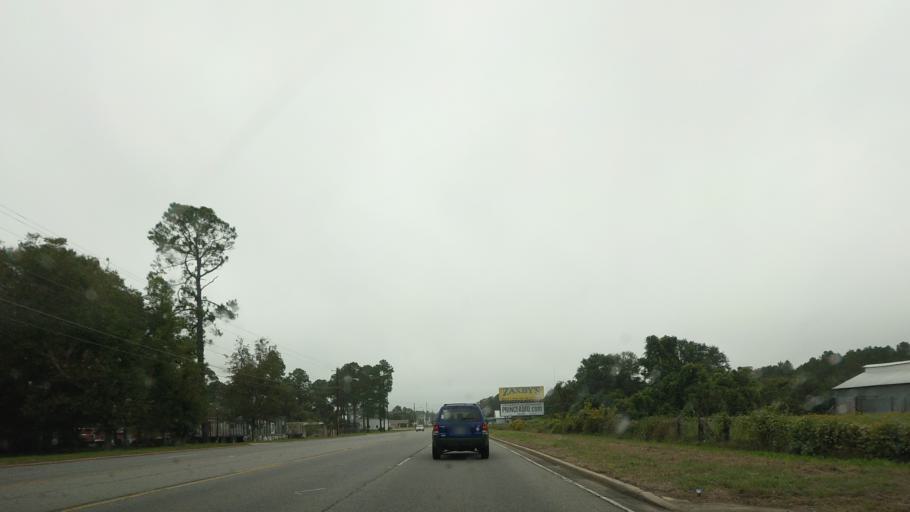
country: US
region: Georgia
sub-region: Irwin County
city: Ocilla
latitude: 31.6157
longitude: -83.2499
